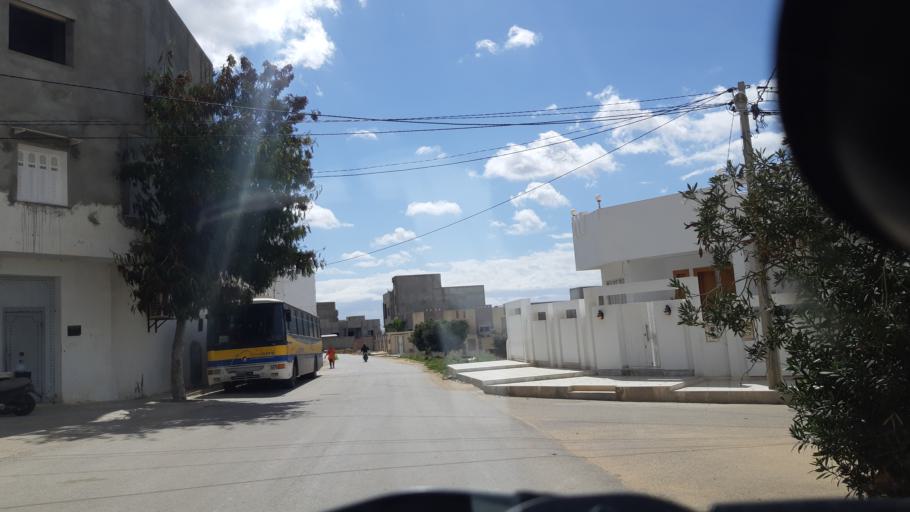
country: TN
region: Susah
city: Akouda
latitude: 35.8807
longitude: 10.5404
